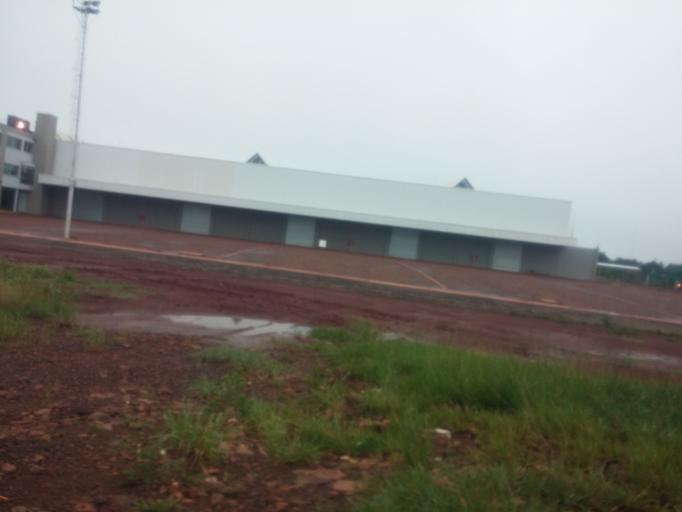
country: AR
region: Misiones
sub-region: Departamento de Obera
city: Obera
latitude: -27.4743
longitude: -55.0864
